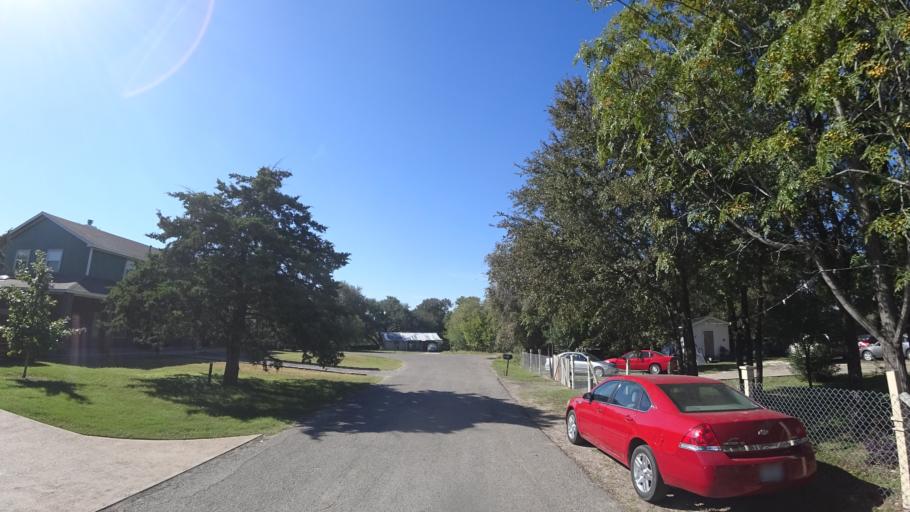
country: US
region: Texas
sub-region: Travis County
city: Hornsby Bend
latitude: 30.2644
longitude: -97.6288
